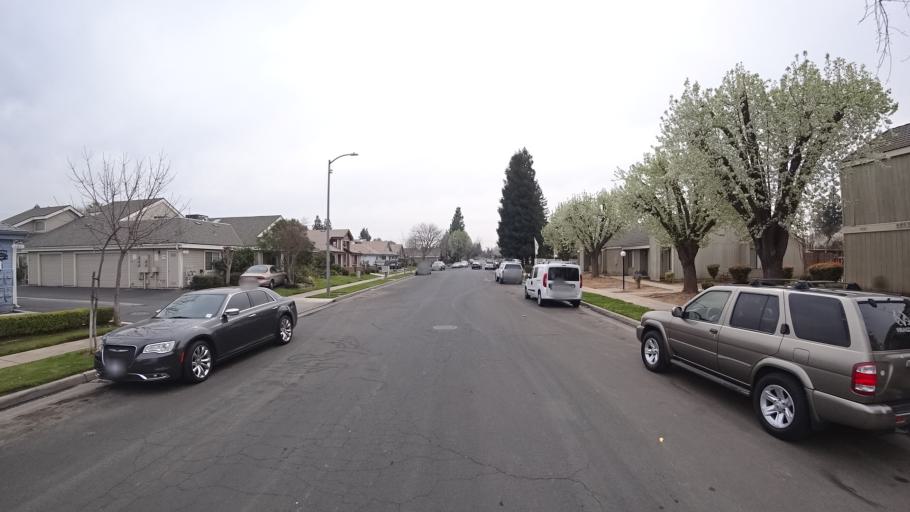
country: US
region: California
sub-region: Fresno County
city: Fresno
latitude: 36.8395
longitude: -119.8130
